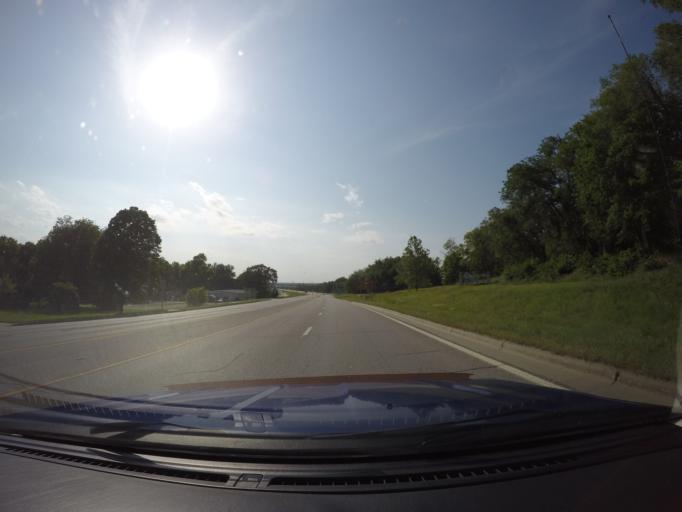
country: US
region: Kansas
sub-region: Riley County
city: Manhattan
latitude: 39.1711
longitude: -96.5441
